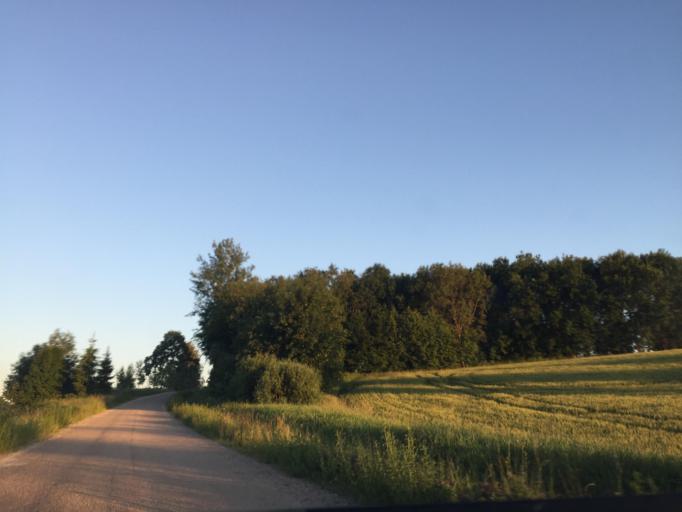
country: LV
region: Rezekne
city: Rezekne
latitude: 56.3654
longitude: 27.4109
